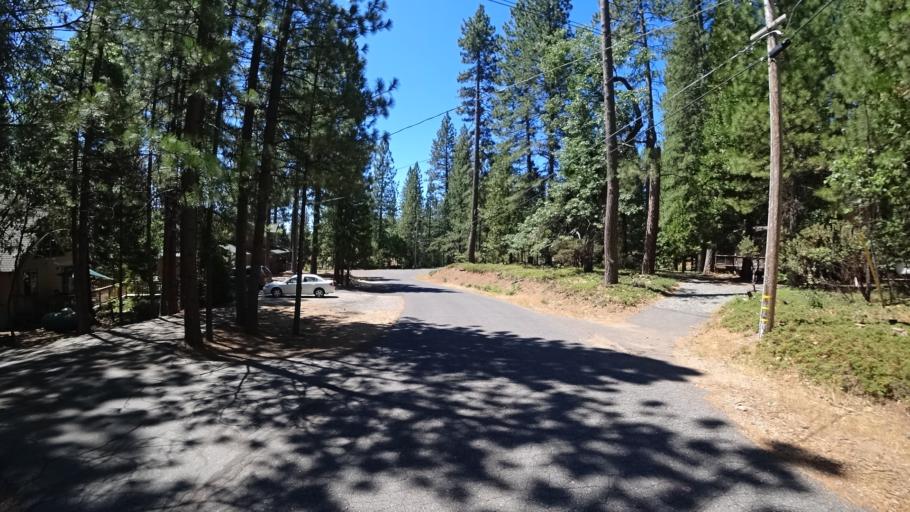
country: US
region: California
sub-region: Calaveras County
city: Arnold
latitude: 38.2260
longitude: -120.3435
